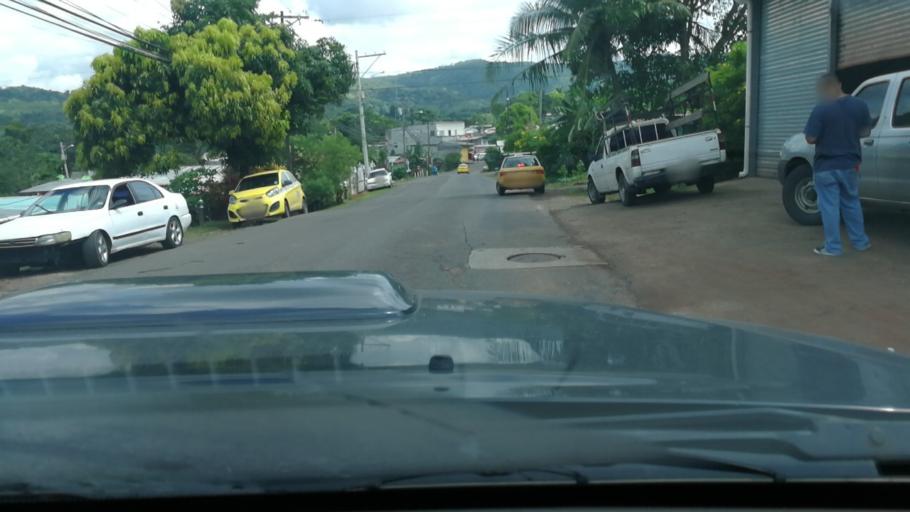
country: PA
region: Panama
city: Tocumen
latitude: 9.0982
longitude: -79.4104
